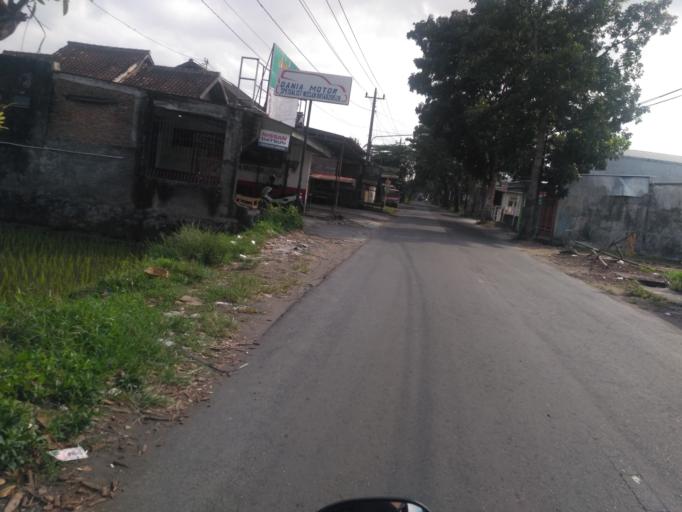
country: ID
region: Daerah Istimewa Yogyakarta
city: Yogyakarta
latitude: -7.7775
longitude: 110.3415
